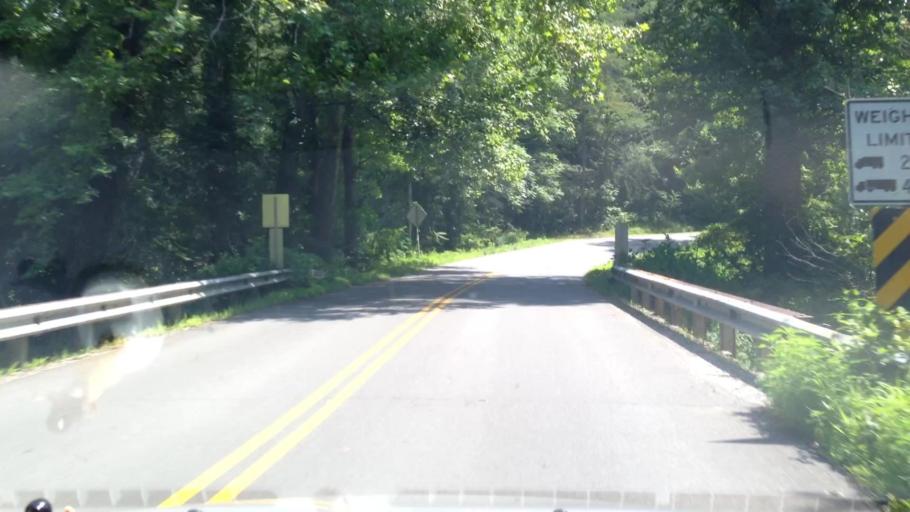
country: US
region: Virginia
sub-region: Patrick County
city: Patrick Springs
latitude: 36.5740
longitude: -80.1995
